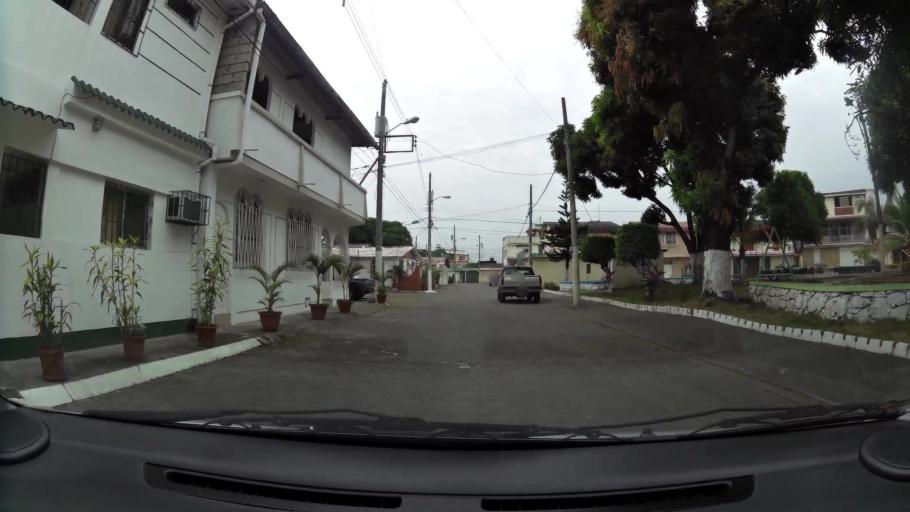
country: EC
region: Guayas
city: Eloy Alfaro
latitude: -2.1336
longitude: -79.8985
